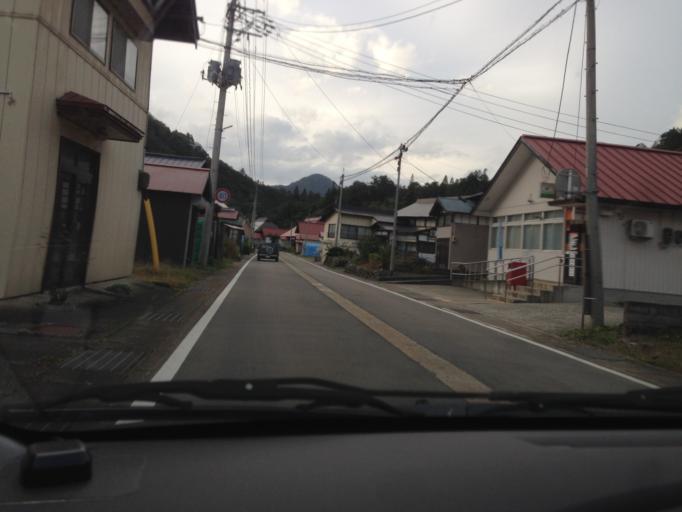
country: JP
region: Fukushima
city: Kitakata
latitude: 37.3635
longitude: 139.5736
